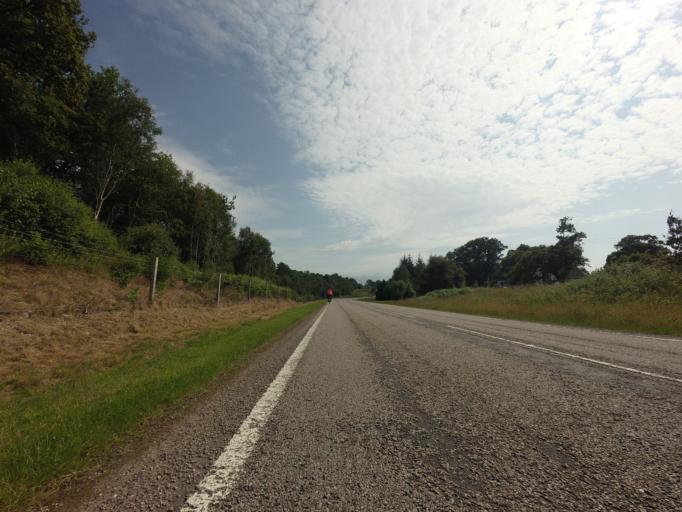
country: GB
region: Scotland
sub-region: Highland
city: Evanton
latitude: 57.9291
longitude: -4.4010
